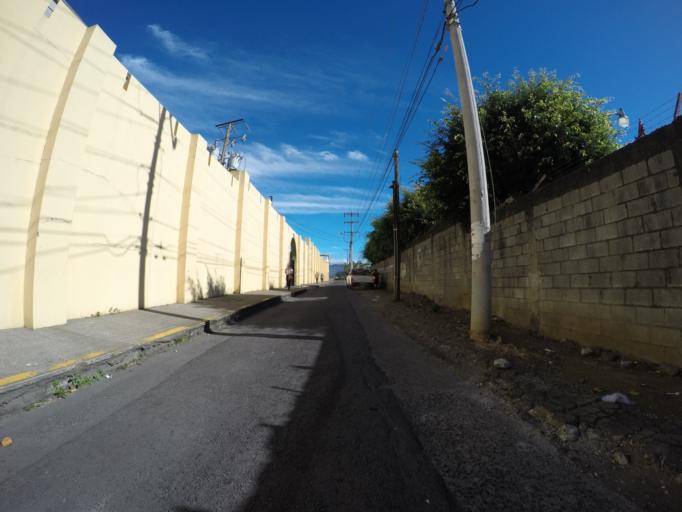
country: CR
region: San Jose
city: San Jose
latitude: 9.9407
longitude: -84.0796
